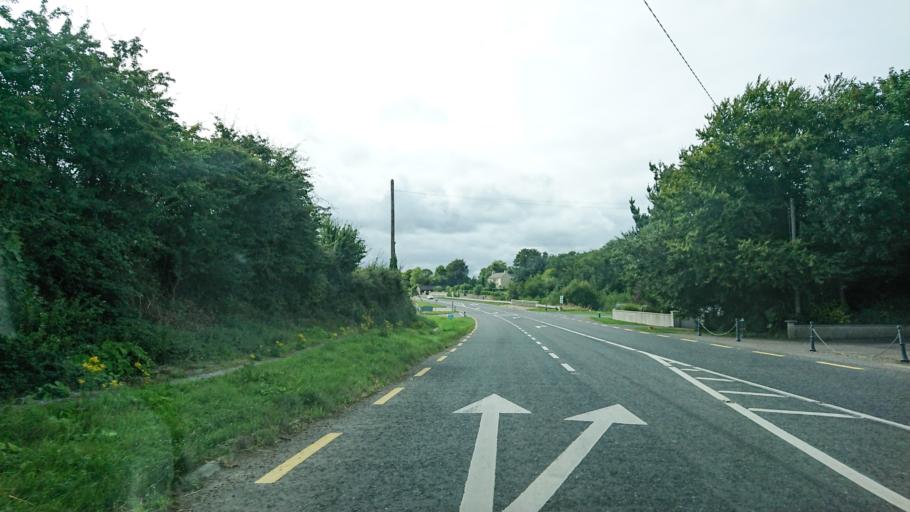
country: IE
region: Munster
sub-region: County Cork
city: Mallow
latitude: 52.1555
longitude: -8.5084
